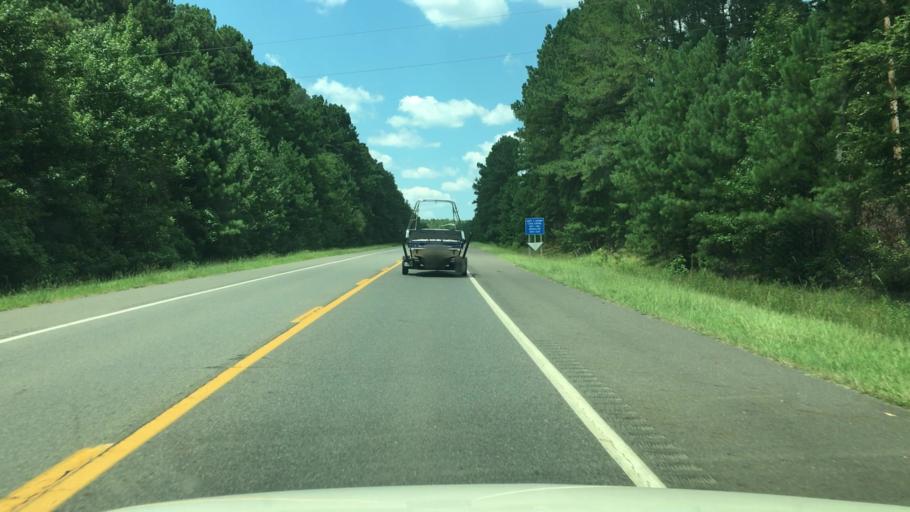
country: US
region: Arkansas
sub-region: Clark County
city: Arkadelphia
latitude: 34.2018
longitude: -93.0780
